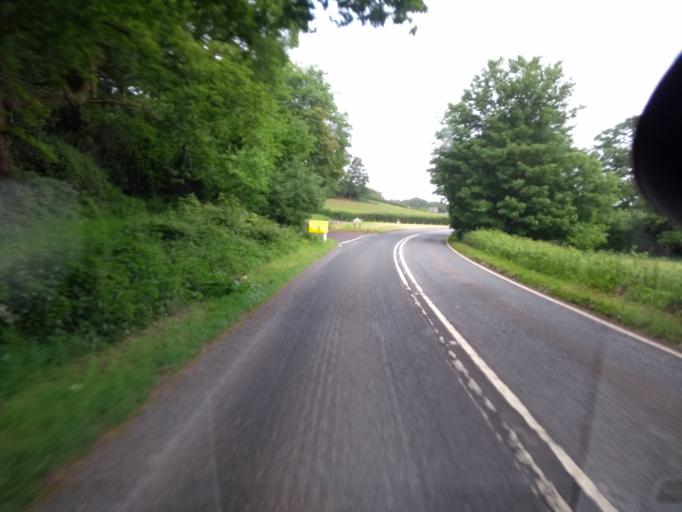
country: GB
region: England
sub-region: Somerset
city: Bishops Lydeard
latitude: 51.1592
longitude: -3.2059
